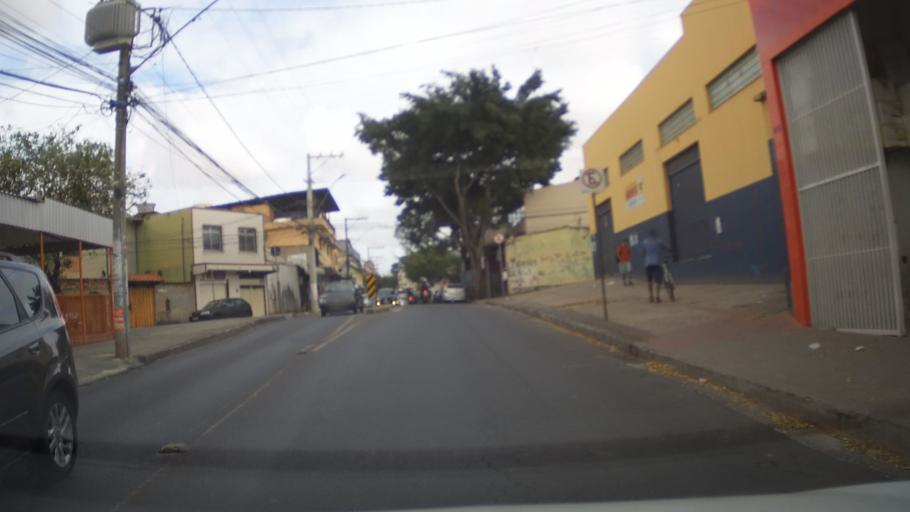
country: BR
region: Minas Gerais
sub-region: Belo Horizonte
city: Belo Horizonte
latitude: -19.8422
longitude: -43.9488
